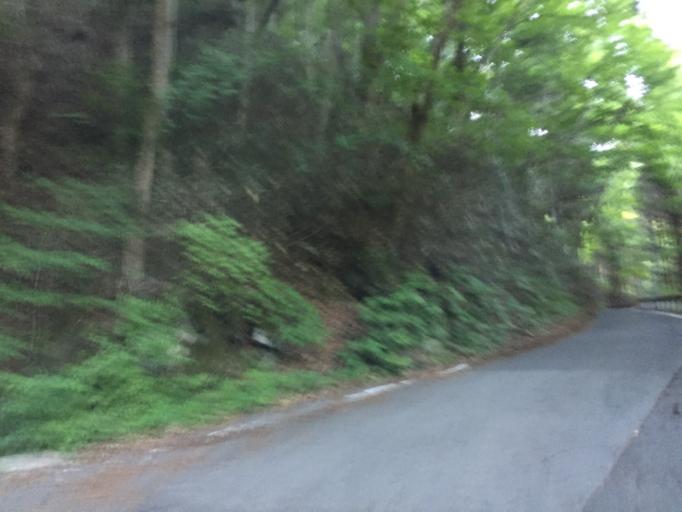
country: JP
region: Ibaraki
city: Kitaibaraki
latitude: 36.8895
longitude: 140.6227
